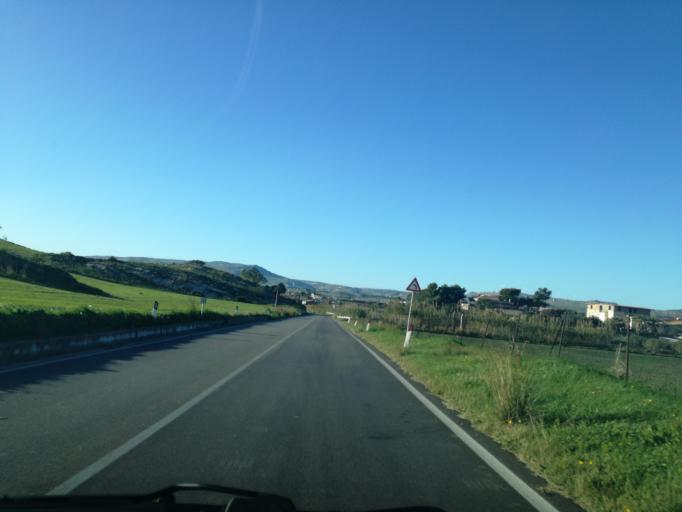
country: IT
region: Sicily
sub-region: Provincia di Caltanissetta
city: Butera
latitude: 37.1130
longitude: 14.1492
